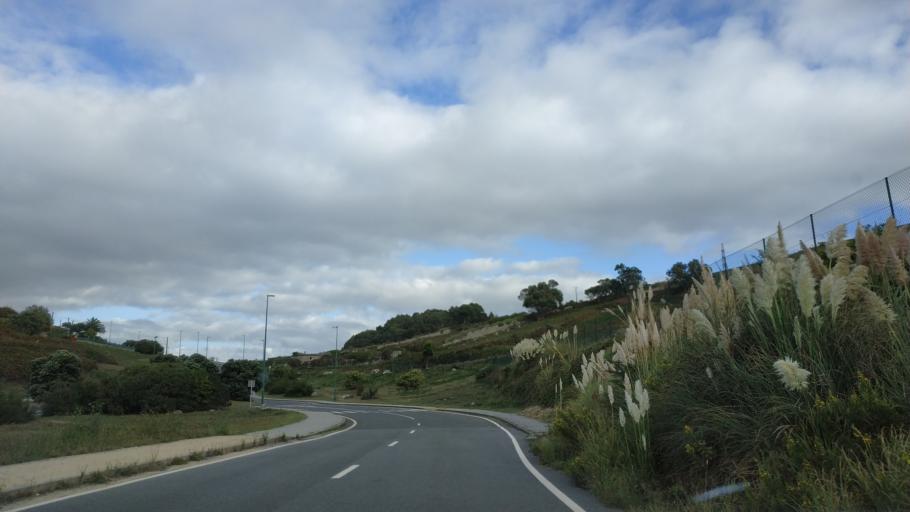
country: ES
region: Galicia
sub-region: Provincia da Coruna
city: A Coruna
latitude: 43.3706
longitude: -8.4446
